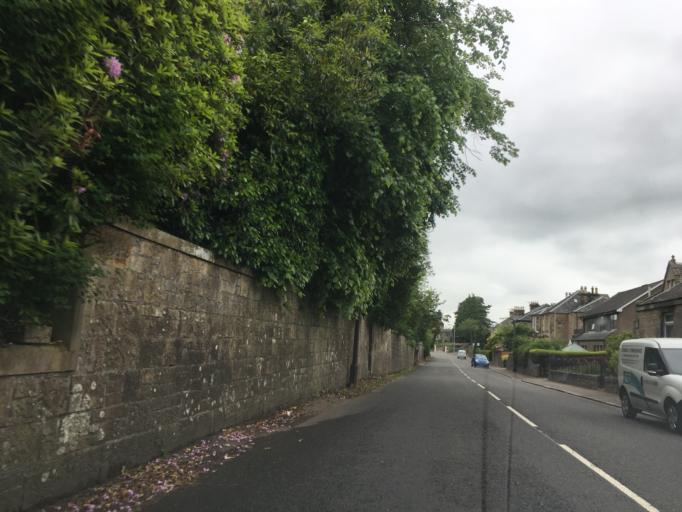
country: GB
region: Scotland
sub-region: Stirling
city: Stirling
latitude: 56.1119
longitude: -3.9535
